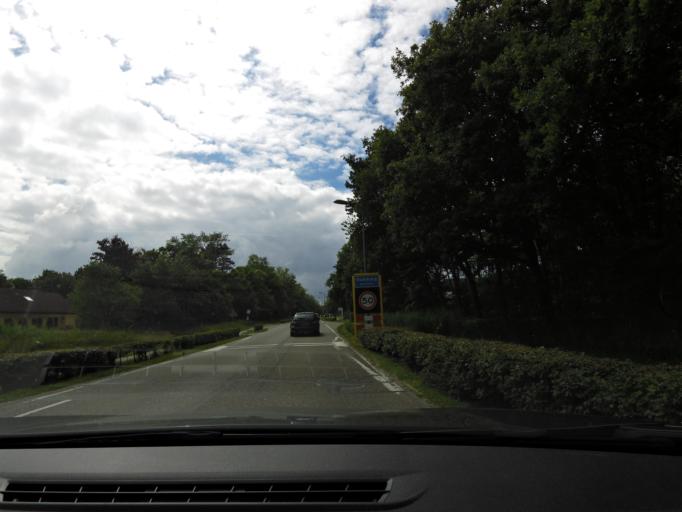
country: NL
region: Zeeland
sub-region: Gemeente Middelburg
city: Middelburg
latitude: 51.5660
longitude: 3.5096
